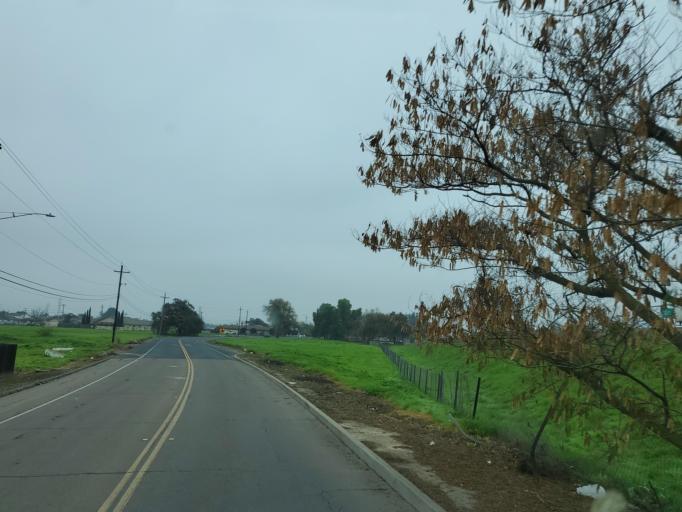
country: US
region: California
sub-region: San Joaquin County
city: Taft Mosswood
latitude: 37.9152
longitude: -121.2896
